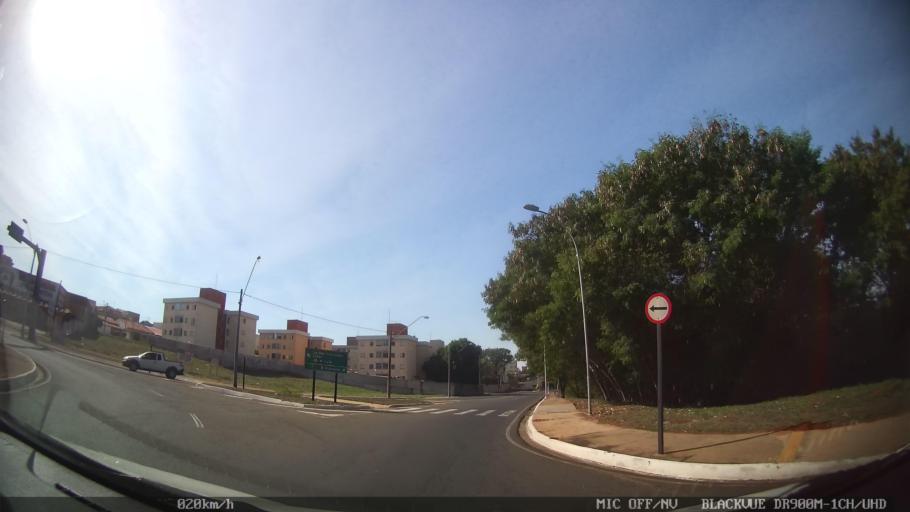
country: BR
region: Sao Paulo
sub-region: Sao Jose Do Rio Preto
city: Sao Jose do Rio Preto
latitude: -20.8014
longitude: -49.4072
